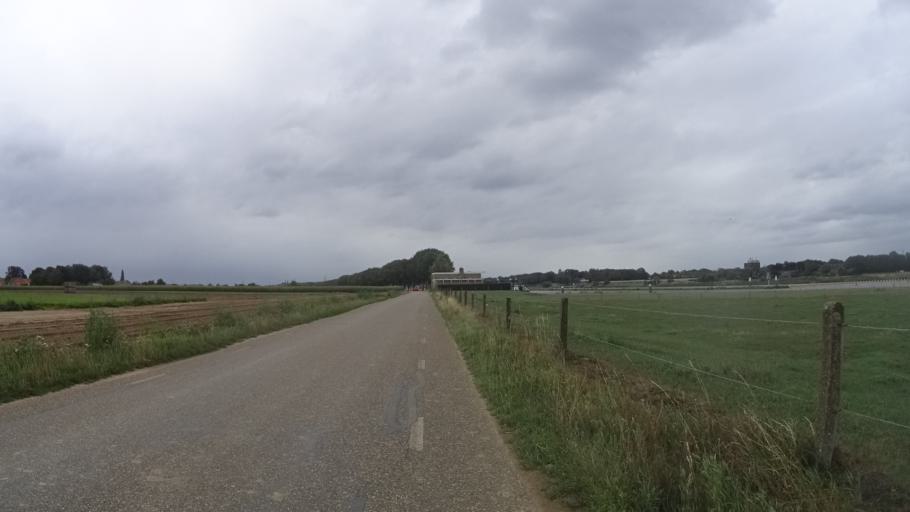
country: NL
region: Limburg
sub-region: Gemeente Beesel
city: Offenbeek
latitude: 51.3144
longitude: 6.1030
